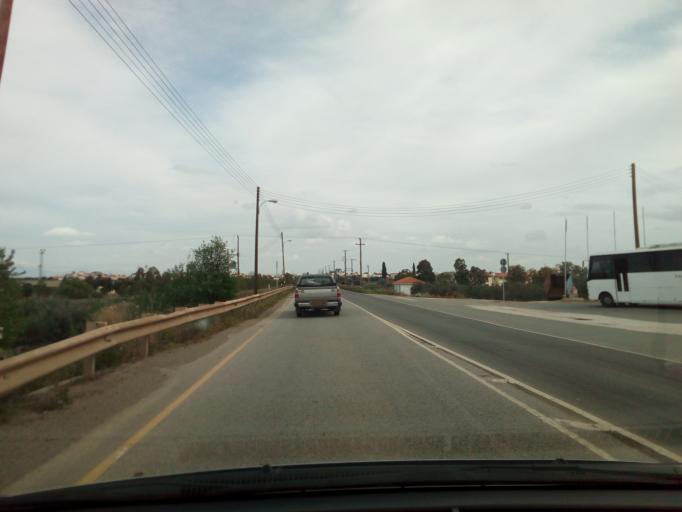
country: CY
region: Lefkosia
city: Akaki
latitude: 35.1355
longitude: 33.1209
